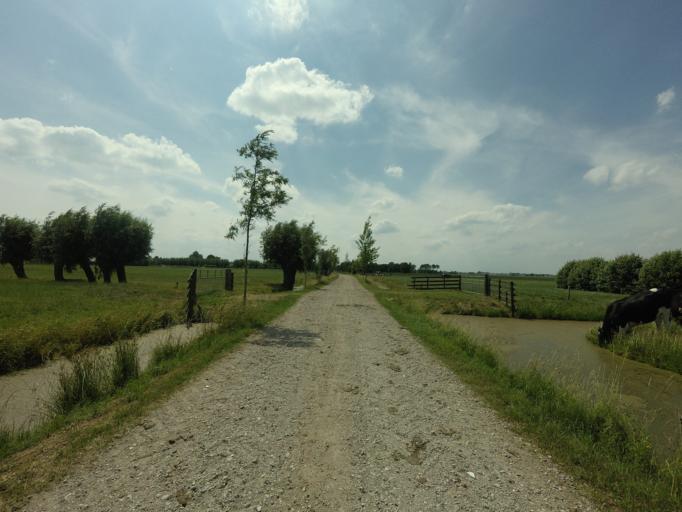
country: NL
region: Utrecht
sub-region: Gemeente Lopik
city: Lopik
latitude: 51.9503
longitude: 4.9140
